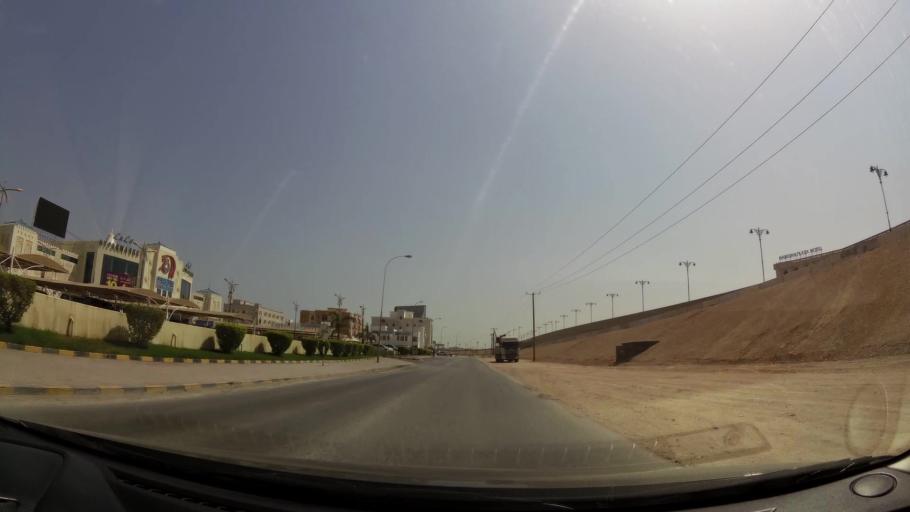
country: OM
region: Zufar
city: Salalah
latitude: 17.0186
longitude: 54.0619
